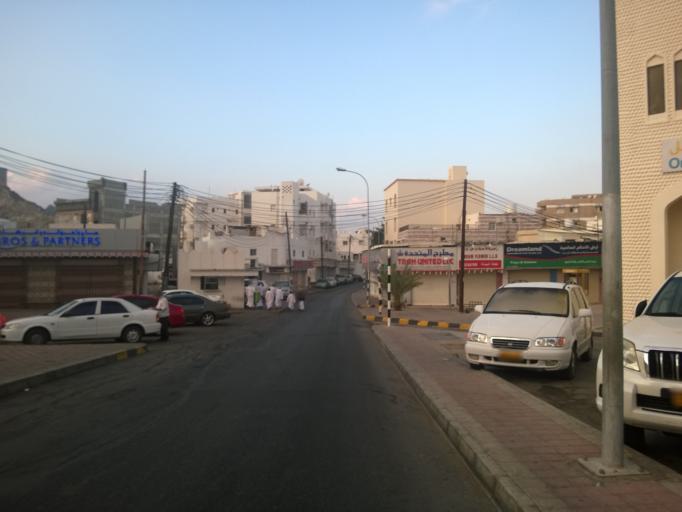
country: OM
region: Muhafazat Masqat
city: Muscat
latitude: 23.6192
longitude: 58.5658
